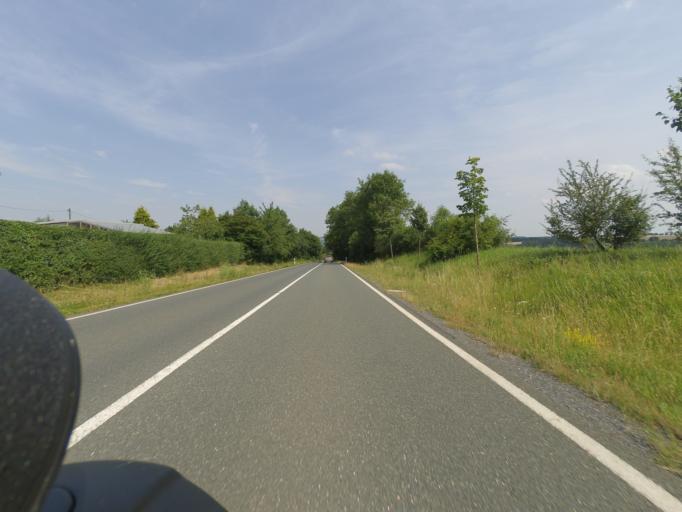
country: DE
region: Thuringia
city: Bad Kostritz
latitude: 50.9249
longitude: 11.9855
